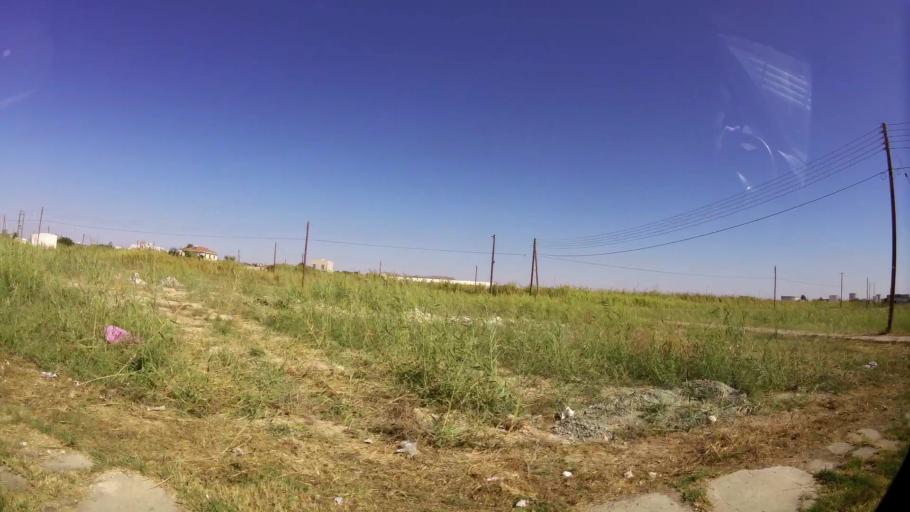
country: CY
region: Larnaka
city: Livadia
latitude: 34.9378
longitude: 33.6315
